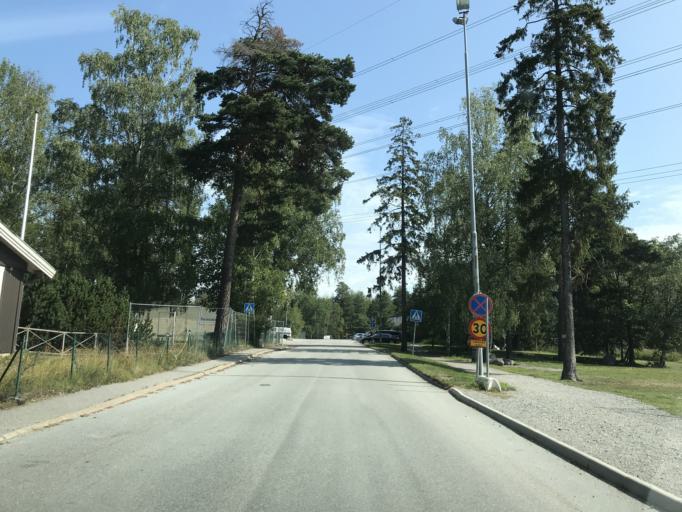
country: SE
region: Stockholm
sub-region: Solna Kommun
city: Rasunda
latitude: 59.3820
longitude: 17.9879
